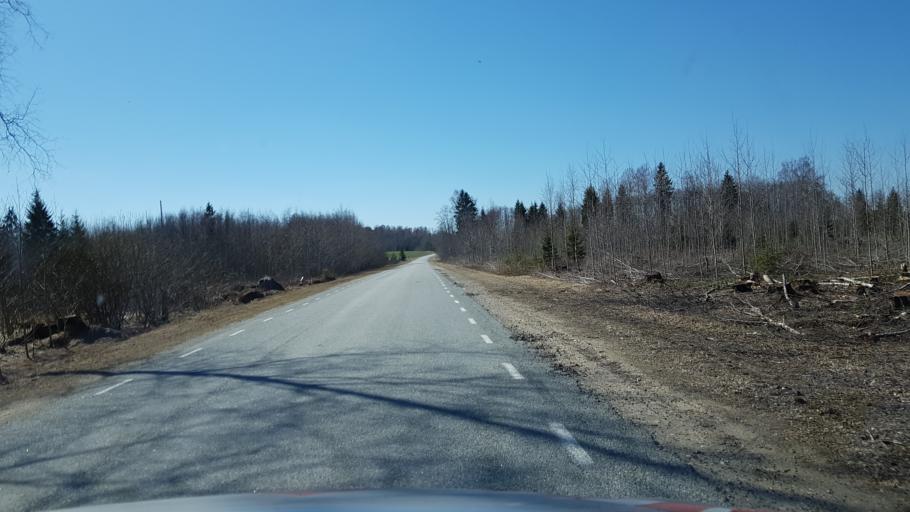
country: EE
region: Laeaene-Virumaa
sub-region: Rakke vald
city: Rakke
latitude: 59.0112
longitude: 26.3363
